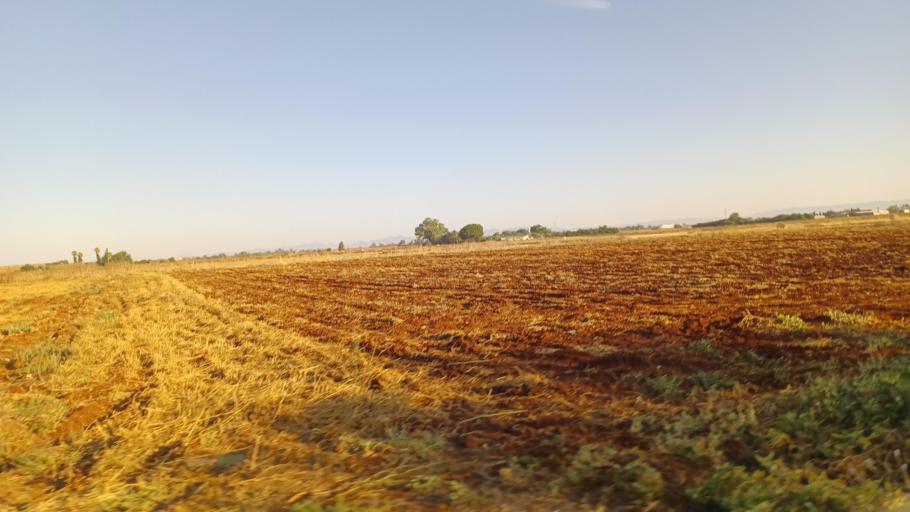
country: CY
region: Ammochostos
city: Avgorou
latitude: 35.0060
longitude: 33.8298
